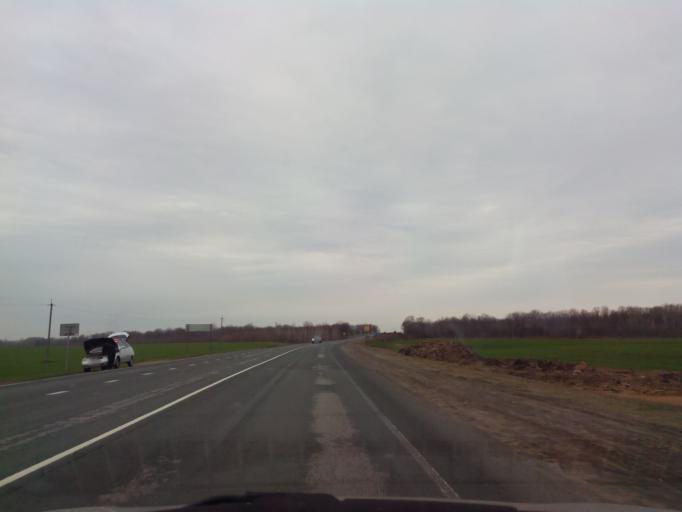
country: RU
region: Tambov
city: Zavoronezhskoye
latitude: 52.9116
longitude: 40.6316
